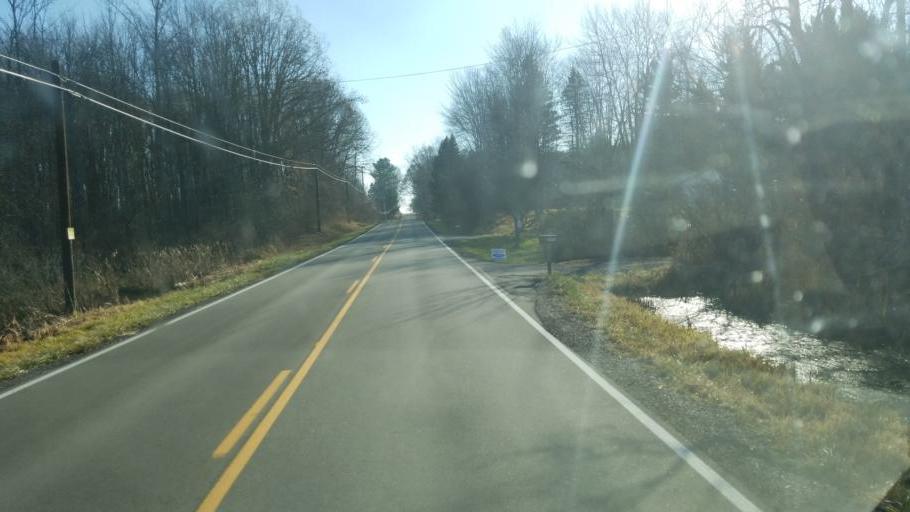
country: US
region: Ohio
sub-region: Portage County
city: Mantua
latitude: 41.3603
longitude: -81.2459
